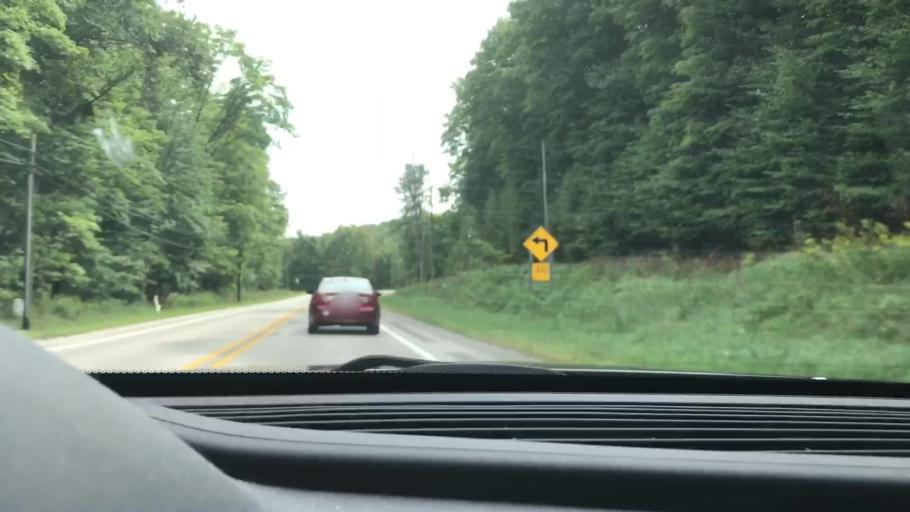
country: US
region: Michigan
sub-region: Antrim County
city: Bellaire
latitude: 45.0809
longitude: -85.2840
